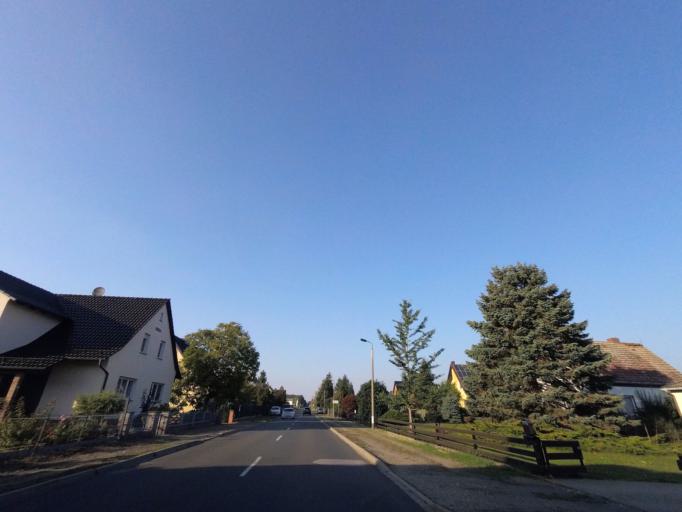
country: DE
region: Saxony-Anhalt
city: Jessen
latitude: 51.7948
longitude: 12.9546
